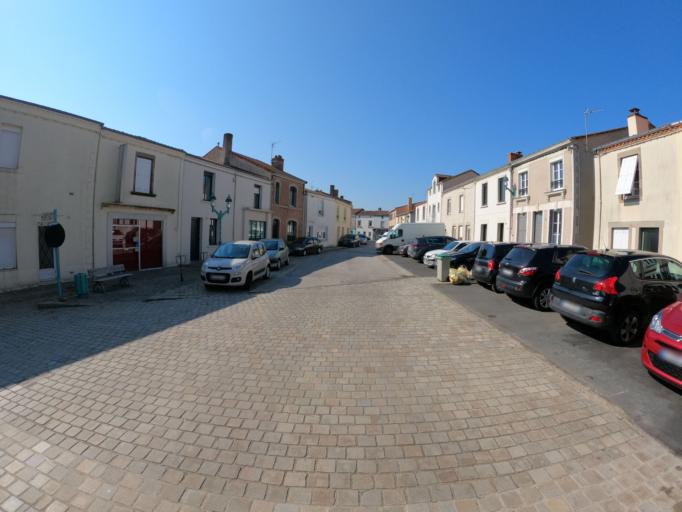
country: FR
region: Pays de la Loire
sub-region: Departement de la Loire-Atlantique
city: Aigrefeuille-sur-Maine
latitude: 47.0773
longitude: -1.3992
